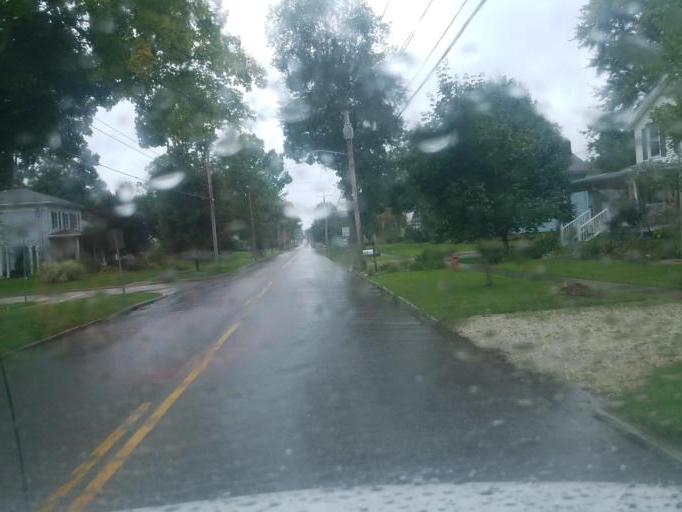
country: US
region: Ohio
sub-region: Medina County
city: Seville
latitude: 41.0101
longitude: -81.8573
